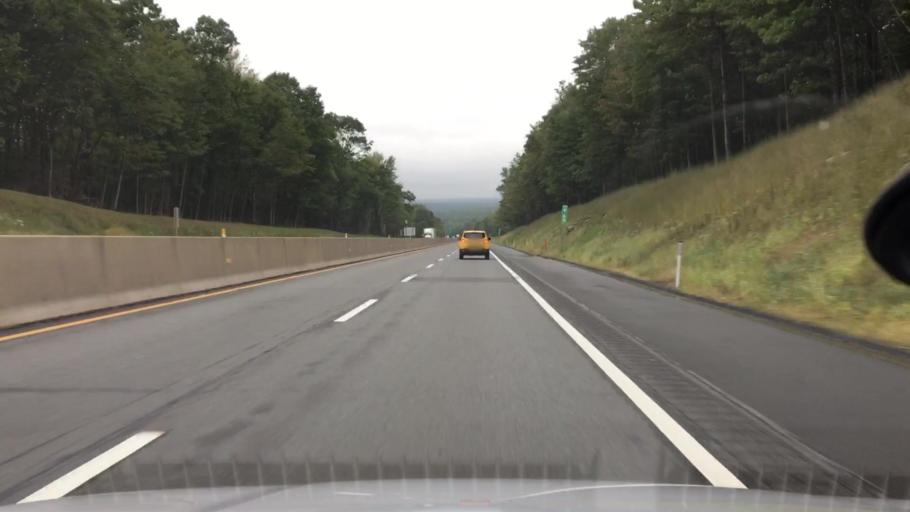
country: US
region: Pennsylvania
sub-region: Luzerne County
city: White Haven
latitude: 41.0892
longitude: -75.7391
